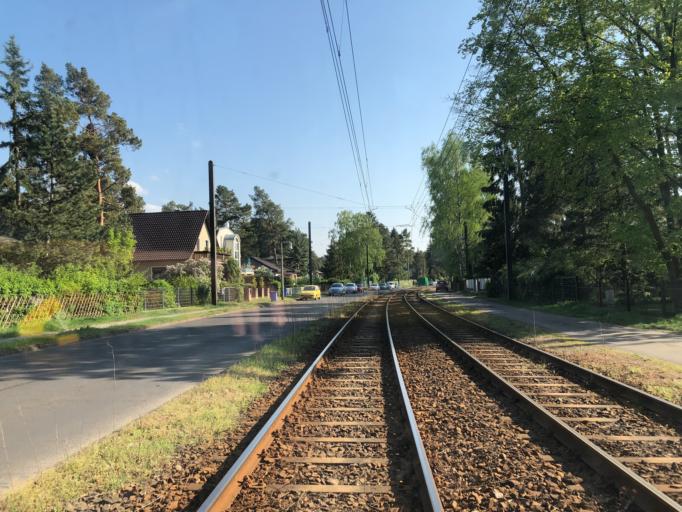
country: DE
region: Berlin
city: Schmockwitz
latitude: 52.3897
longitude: 13.6352
